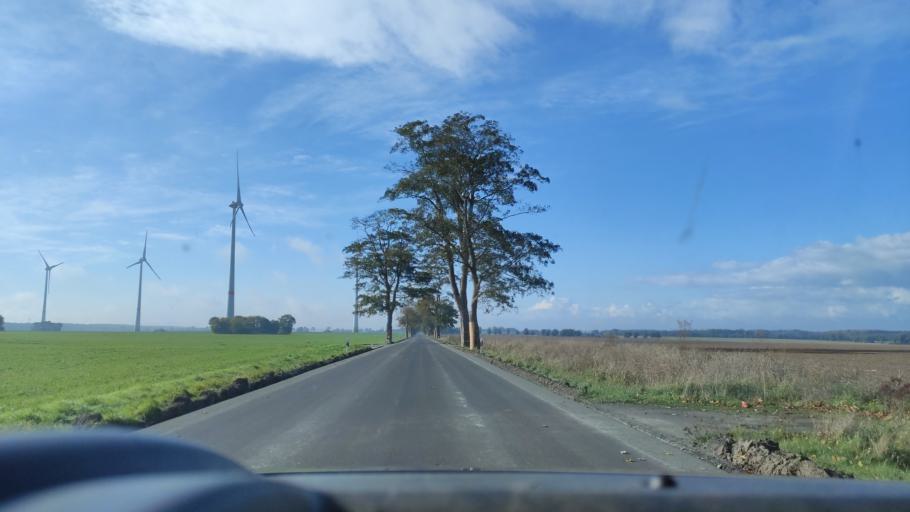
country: DE
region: Mecklenburg-Vorpommern
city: Grimmen
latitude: 54.0580
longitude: 13.1554
